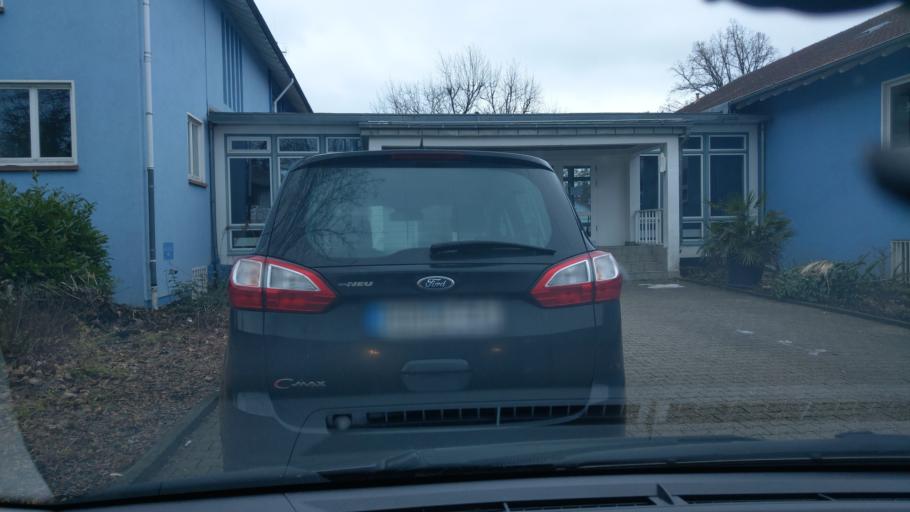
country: DE
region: Saarland
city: Ottweiler
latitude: 49.3724
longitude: 7.1698
